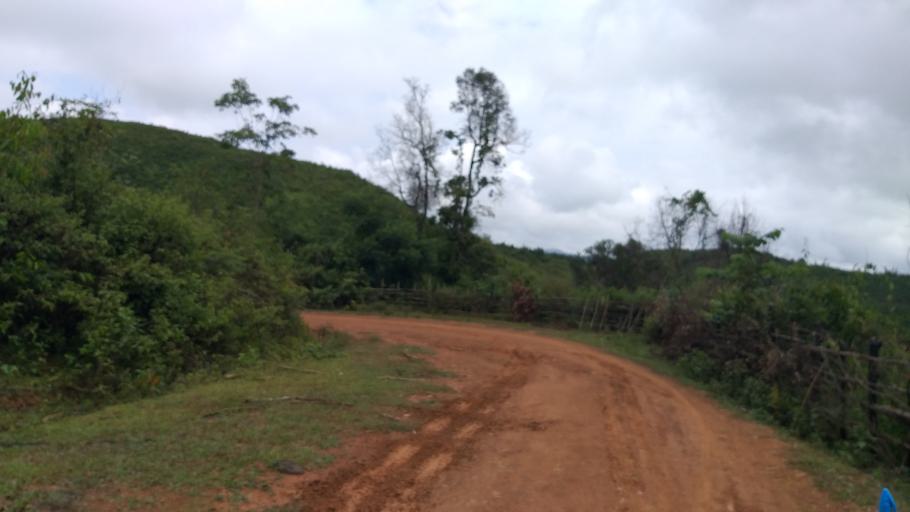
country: LA
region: Phongsali
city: Khoa
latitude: 21.3639
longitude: 102.6231
